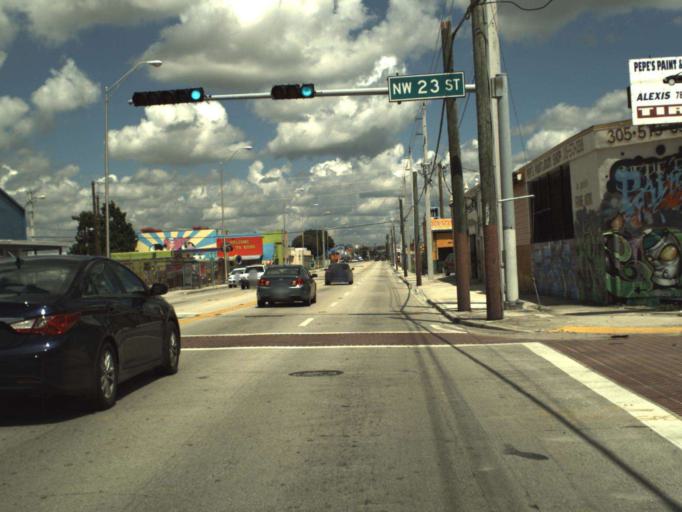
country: US
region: Florida
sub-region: Miami-Dade County
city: Allapattah
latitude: 25.7989
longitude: -80.2071
